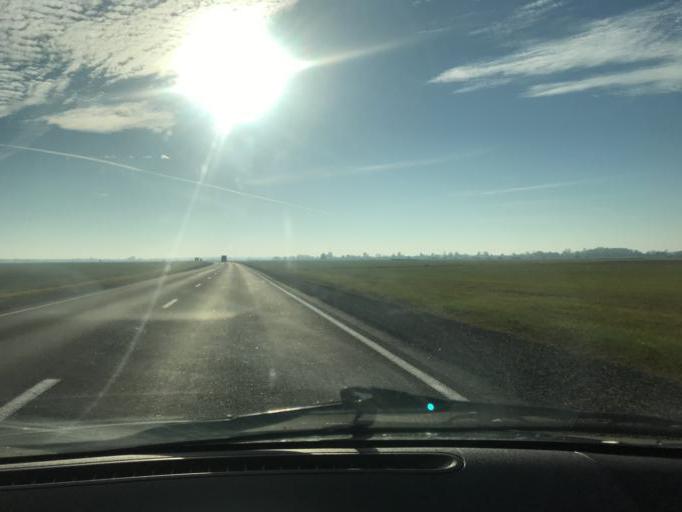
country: BY
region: Brest
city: Drahichyn
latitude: 52.1990
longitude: 25.2370
